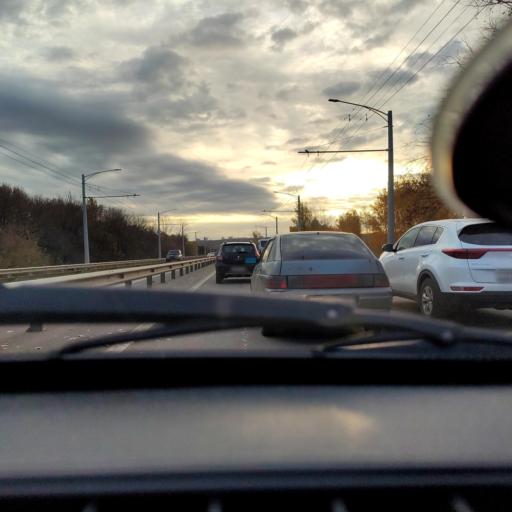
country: RU
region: Bashkortostan
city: Ufa
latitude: 54.7677
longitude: 55.9270
